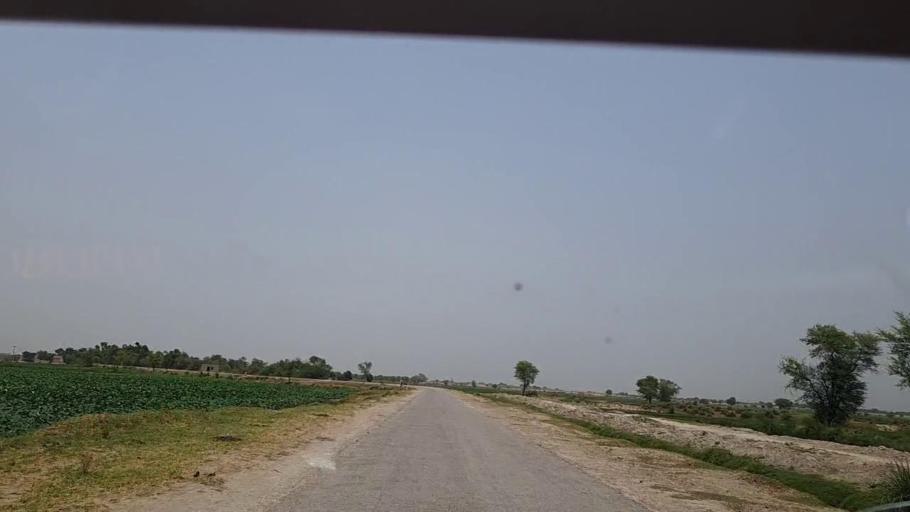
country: PK
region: Sindh
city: Khairpur Nathan Shah
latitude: 27.0128
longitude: 67.6706
